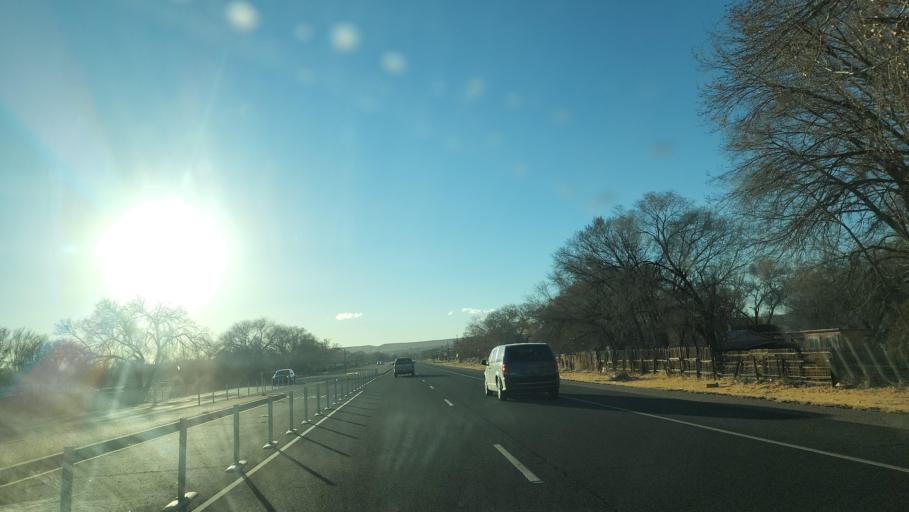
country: US
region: New Mexico
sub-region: Bernalillo County
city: South Valley
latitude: 35.0269
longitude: -106.6956
